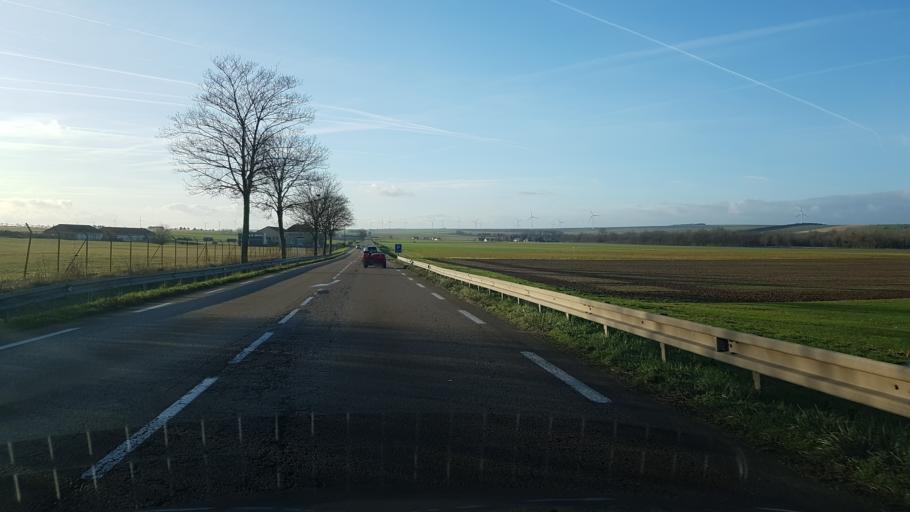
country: FR
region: Champagne-Ardenne
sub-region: Departement de la Marne
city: Vitry-le-Francois
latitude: 48.7438
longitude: 4.5199
